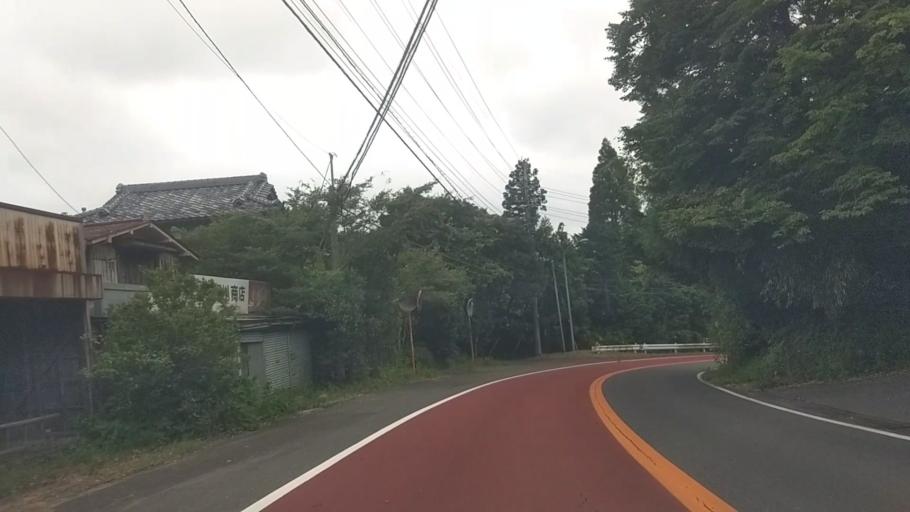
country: JP
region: Chiba
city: Kawaguchi
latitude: 35.2256
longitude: 140.0744
